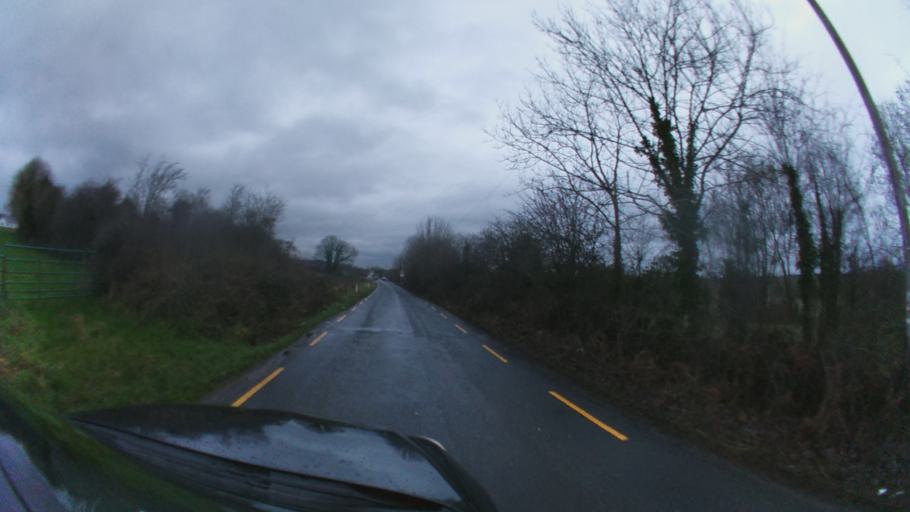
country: IE
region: Leinster
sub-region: Kilkenny
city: Graiguenamanagh
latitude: 52.5865
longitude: -6.9593
